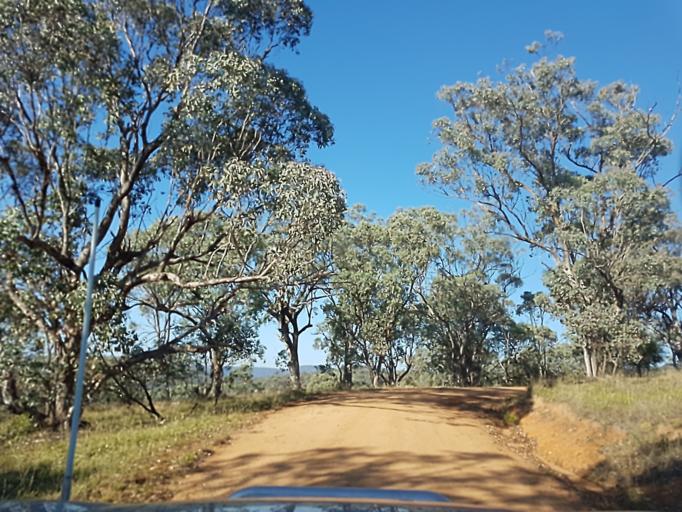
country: AU
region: New South Wales
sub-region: Snowy River
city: Jindabyne
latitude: -36.9560
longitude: 148.3616
